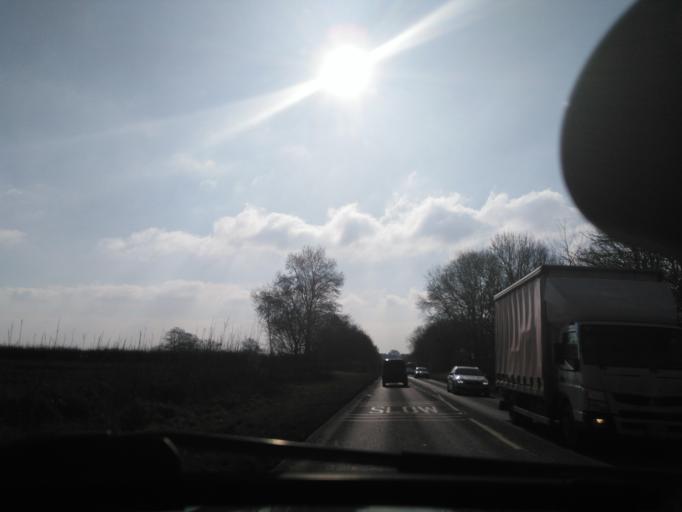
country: GB
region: England
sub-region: Wiltshire
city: Malmesbury
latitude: 51.5876
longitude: -2.0886
